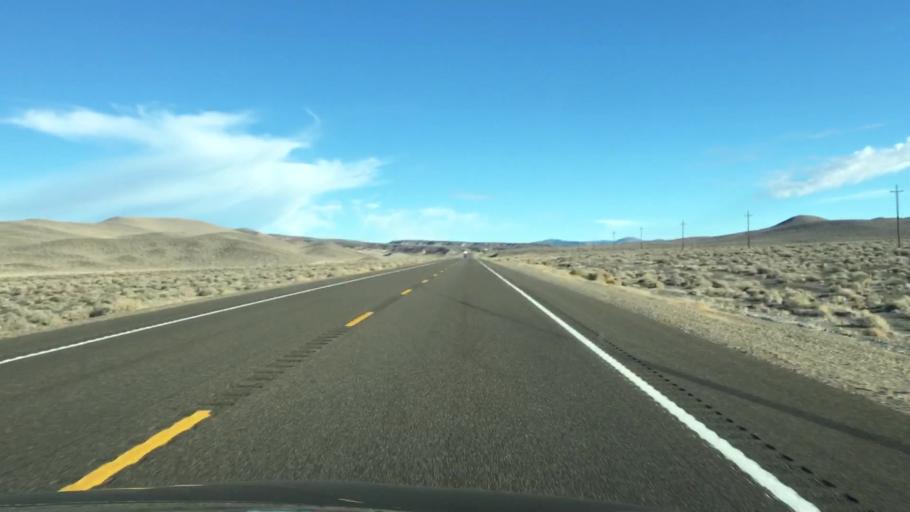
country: US
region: Nevada
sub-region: Mineral County
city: Hawthorne
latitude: 38.2401
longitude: -118.0392
